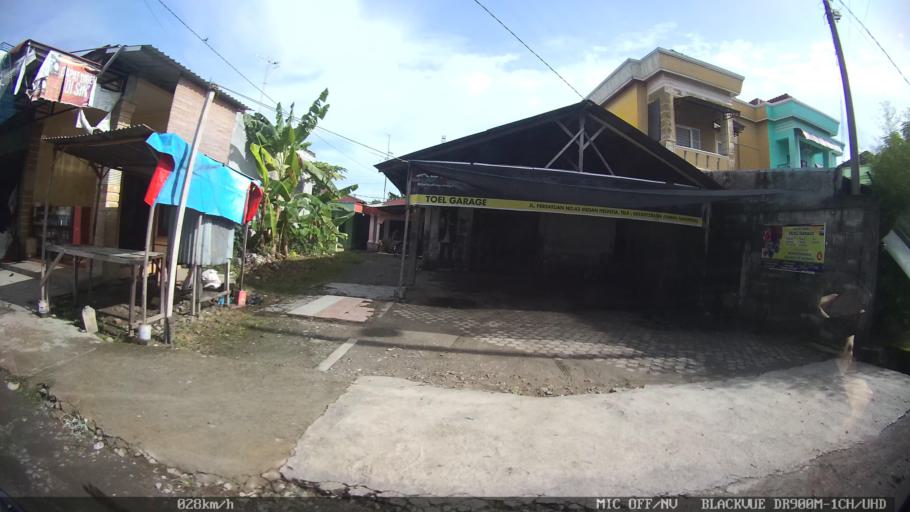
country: ID
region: North Sumatra
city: Medan
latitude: 3.6117
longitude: 98.6520
